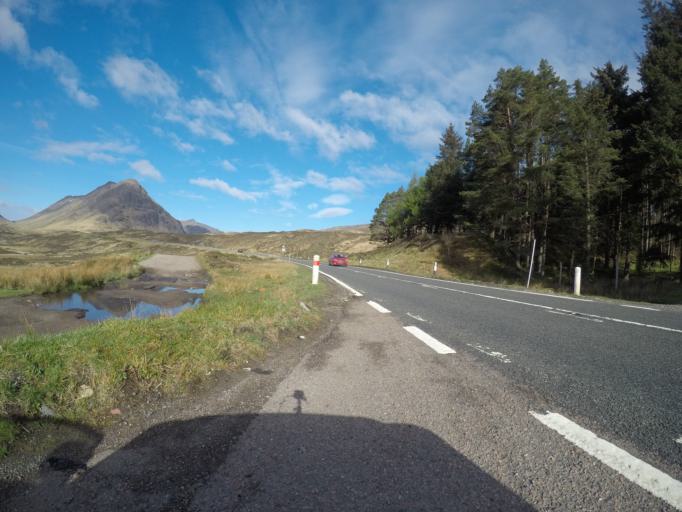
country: GB
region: Scotland
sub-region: Highland
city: Spean Bridge
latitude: 56.6647
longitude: -4.9037
